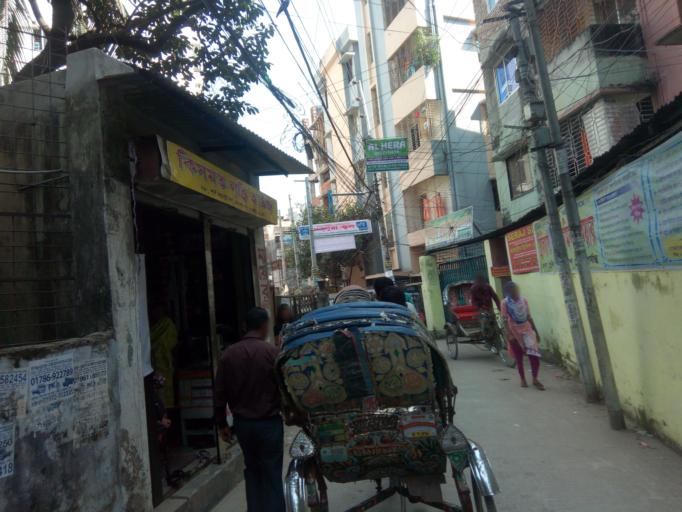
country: BD
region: Dhaka
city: Paltan
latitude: 23.7551
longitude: 90.4128
